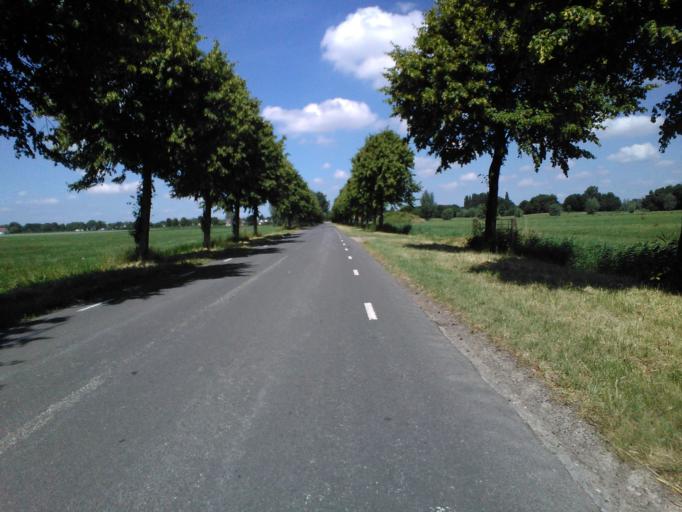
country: NL
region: North Brabant
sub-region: Gemeente Woudrichem
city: Almkerk
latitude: 51.7658
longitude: 4.9711
